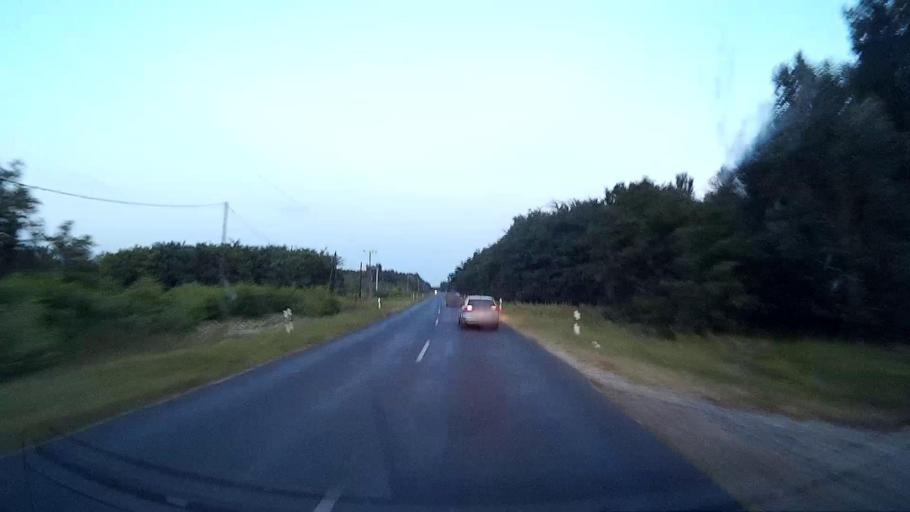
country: HU
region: Pest
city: Cegledbercel
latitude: 47.2049
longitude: 19.6935
